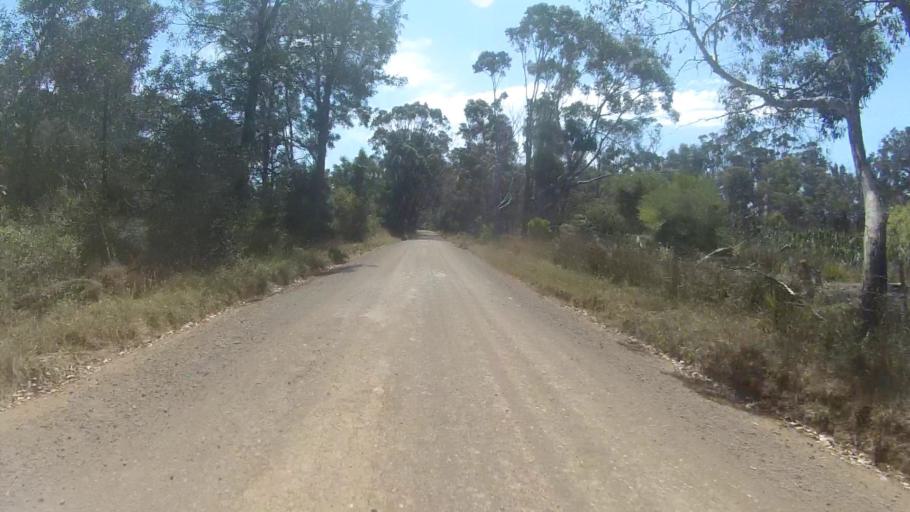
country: AU
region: Tasmania
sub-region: Sorell
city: Sorell
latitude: -42.8570
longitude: 147.8345
